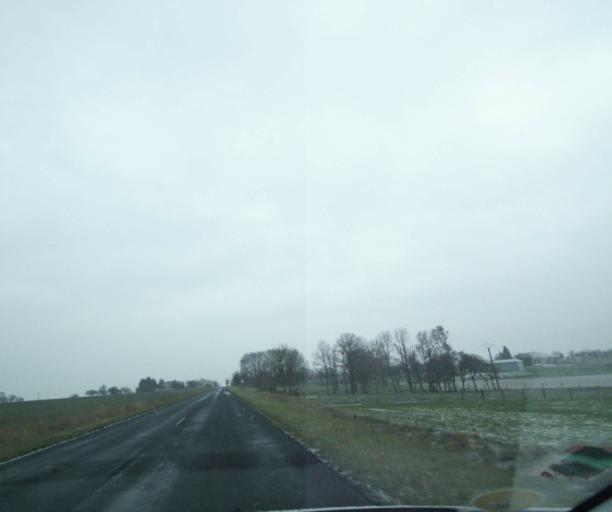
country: FR
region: Champagne-Ardenne
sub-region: Departement de la Haute-Marne
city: Wassy
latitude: 48.4642
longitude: 5.0303
